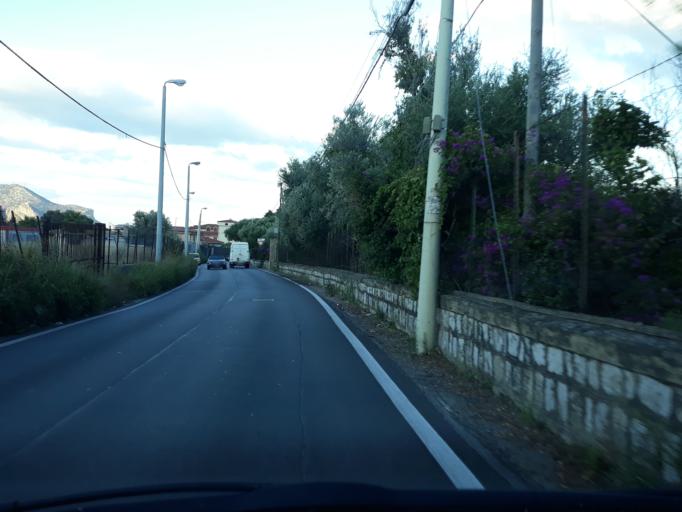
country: IT
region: Sicily
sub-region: Palermo
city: Villa Ciambra
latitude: 38.0851
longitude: 13.3266
